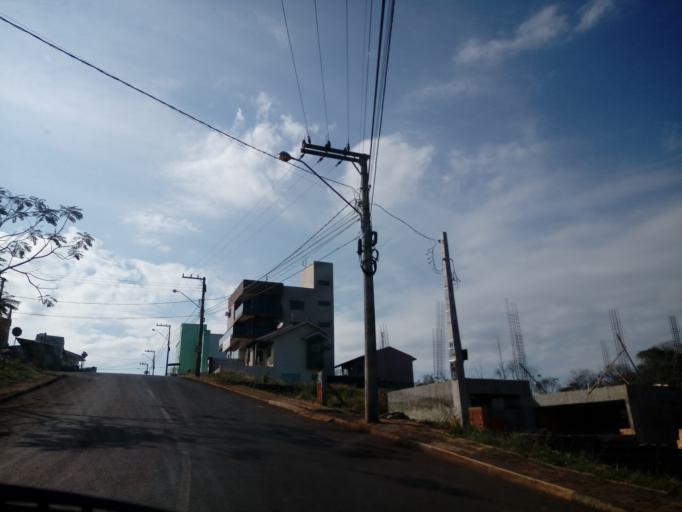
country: BR
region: Santa Catarina
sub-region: Chapeco
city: Chapeco
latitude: -27.1057
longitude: -52.5869
